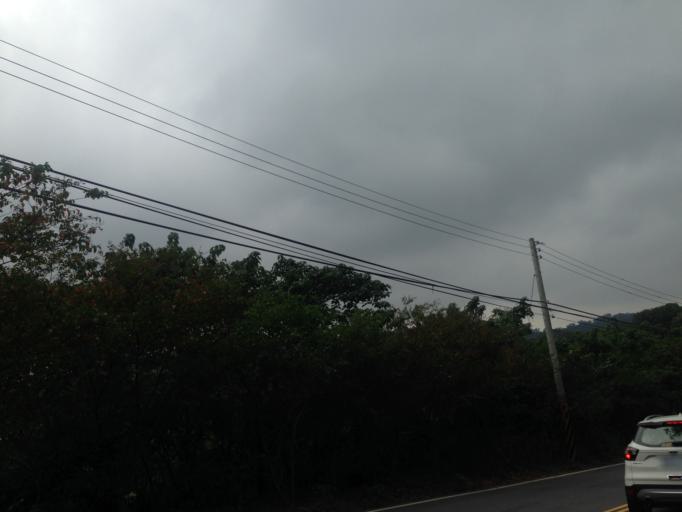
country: TW
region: Taiwan
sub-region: Hsinchu
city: Hsinchu
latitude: 24.6779
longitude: 120.9490
